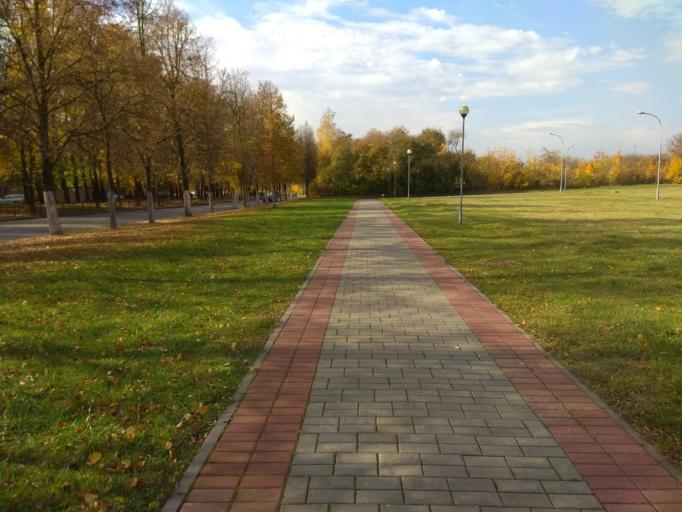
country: BY
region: Grodnenskaya
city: Hrodna
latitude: 53.7093
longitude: 23.7996
